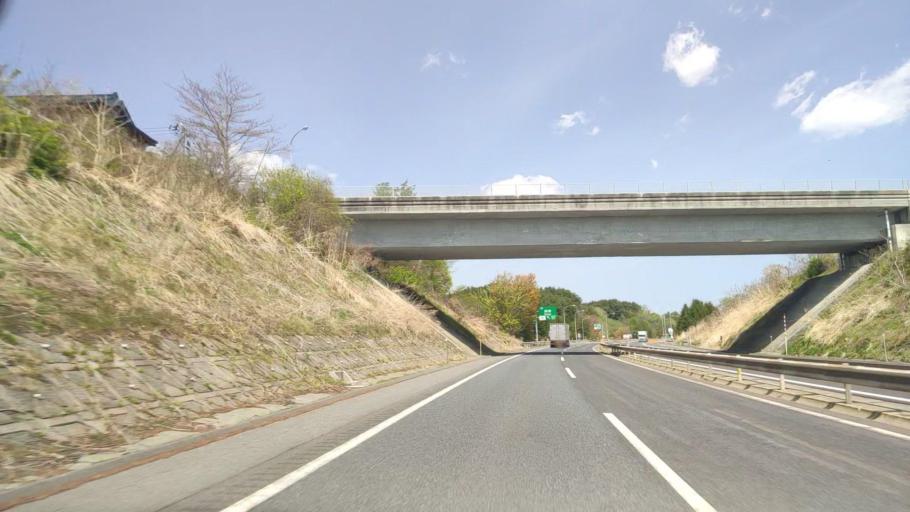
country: JP
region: Aomori
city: Hachinohe
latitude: 40.4028
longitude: 141.4438
